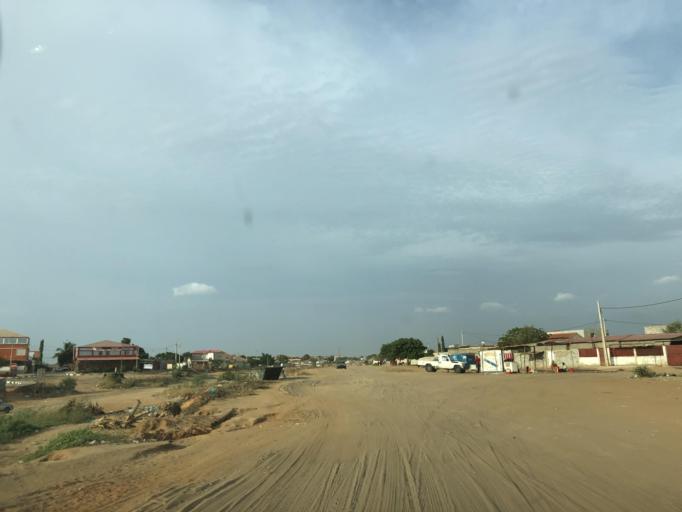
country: AO
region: Luanda
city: Luanda
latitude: -8.9229
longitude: 13.3071
